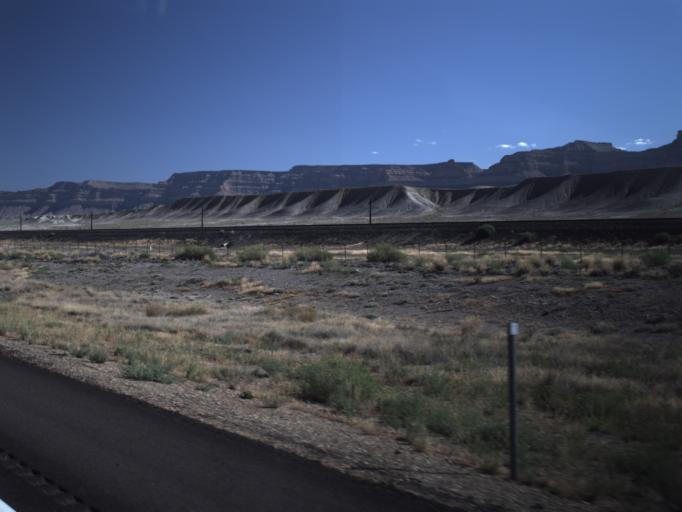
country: US
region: Utah
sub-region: Carbon County
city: East Carbon City
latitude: 39.0447
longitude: -110.3087
